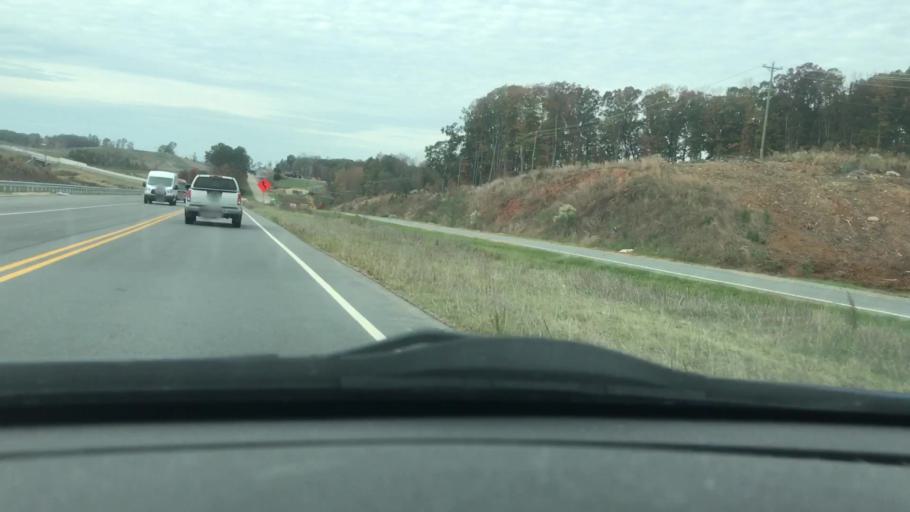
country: US
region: North Carolina
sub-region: Randolph County
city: Asheboro
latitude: 35.6957
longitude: -79.8609
